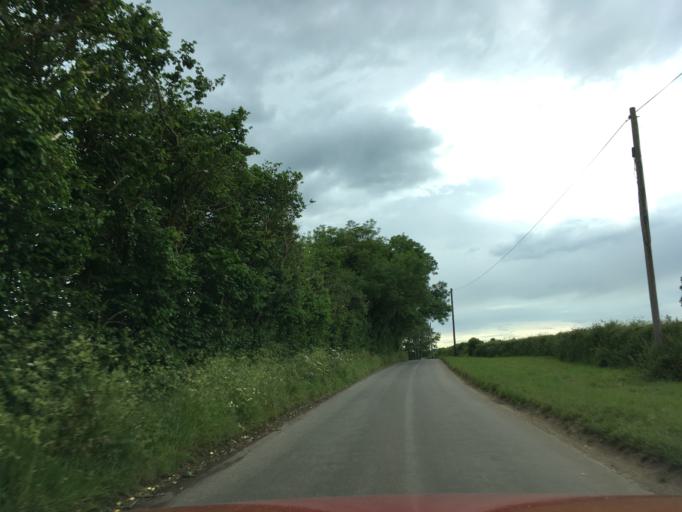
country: GB
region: England
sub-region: Wiltshire
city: Luckington
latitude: 51.5727
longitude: -2.2207
